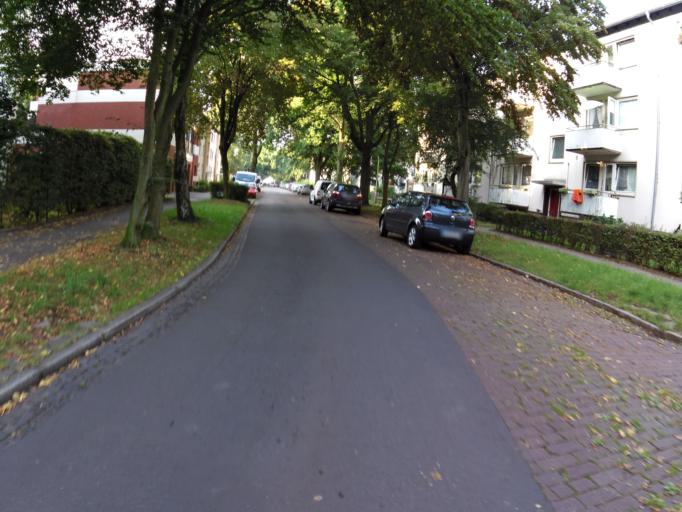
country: DE
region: Bremen
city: Bremen
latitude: 53.0862
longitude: 8.7590
